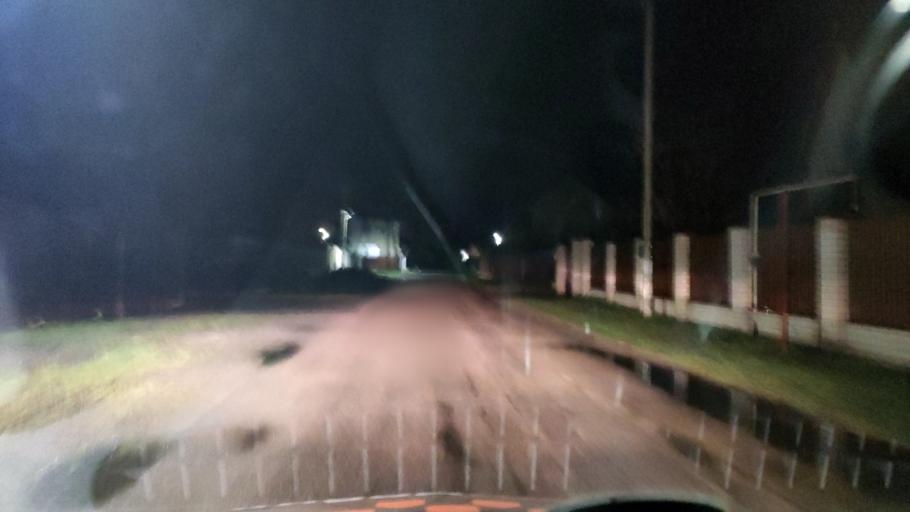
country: RU
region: Voronezj
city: Novaya Usman'
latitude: 51.6097
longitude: 39.4079
